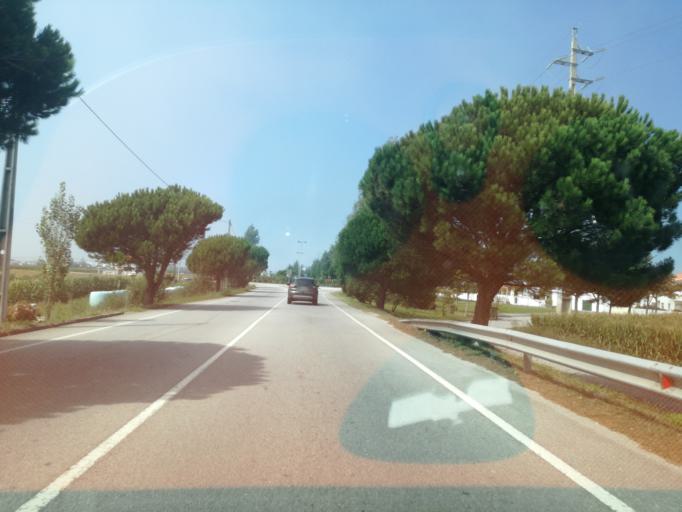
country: PT
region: Braga
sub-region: Esposende
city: Esposende
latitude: 41.5189
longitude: -8.7705
